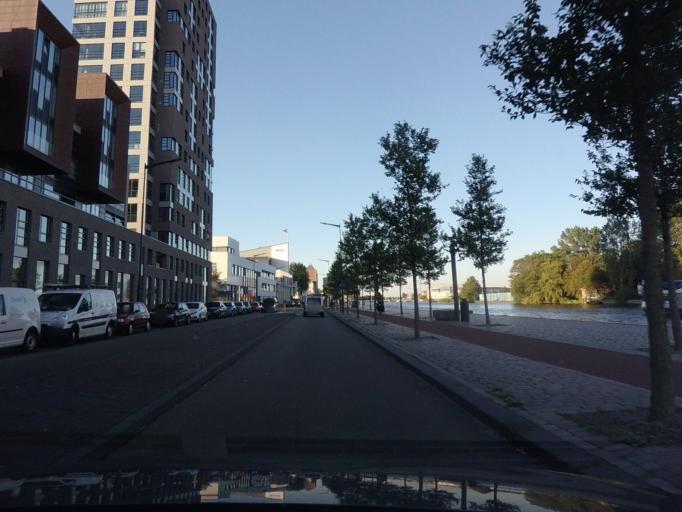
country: NL
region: North Holland
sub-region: Gemeente Haarlem
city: Haarlem
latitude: 52.3894
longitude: 4.6493
